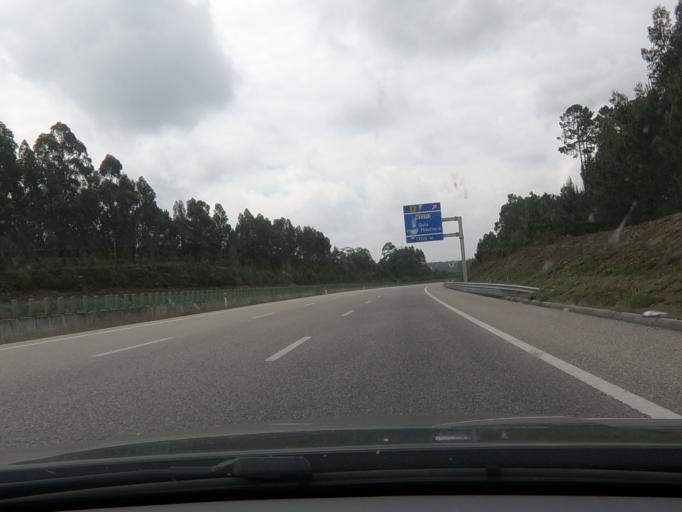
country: PT
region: Leiria
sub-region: Pombal
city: Lourical
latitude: 39.9626
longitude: -8.7761
